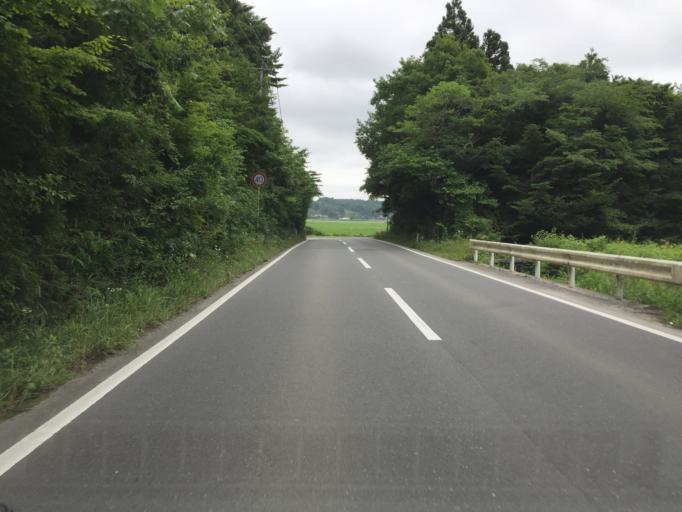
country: JP
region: Miyagi
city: Marumori
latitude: 37.7460
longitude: 140.9154
